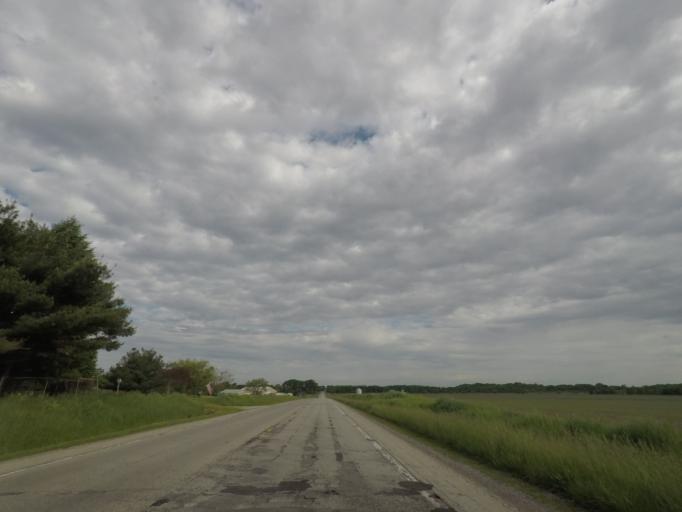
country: US
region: Illinois
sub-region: Logan County
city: Lincoln
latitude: 40.1081
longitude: -89.3253
